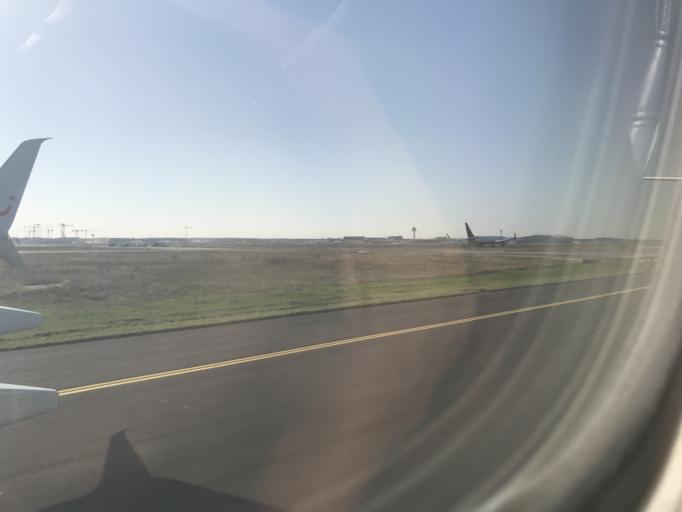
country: DE
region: Hesse
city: Morfelden-Walldorf
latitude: 50.0451
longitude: 8.5786
